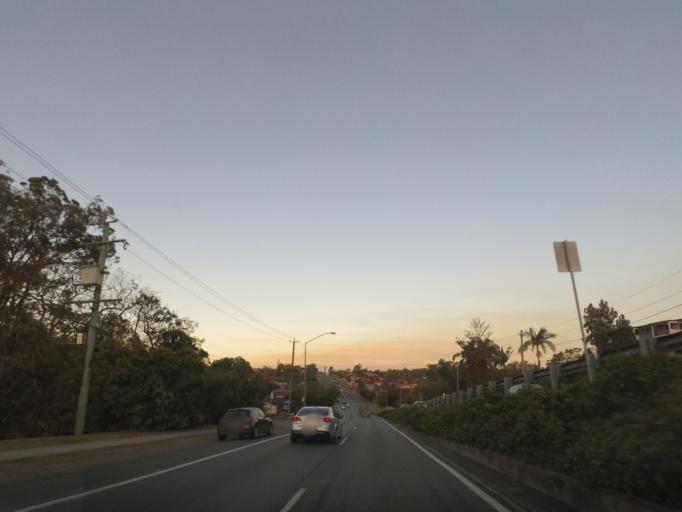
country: AU
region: Queensland
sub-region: Brisbane
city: Upper Mount Gravatt
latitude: -27.5577
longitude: 153.0864
